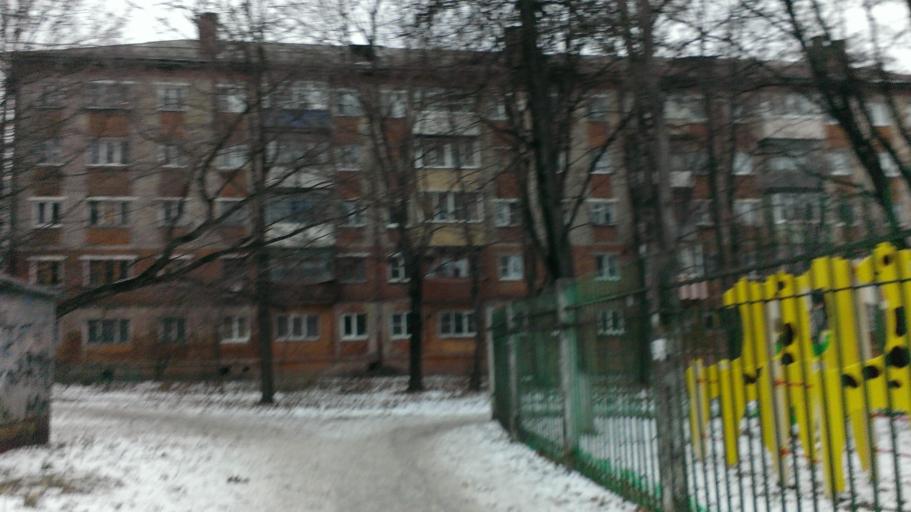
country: RU
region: Tula
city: Tula
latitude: 54.1895
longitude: 37.6964
